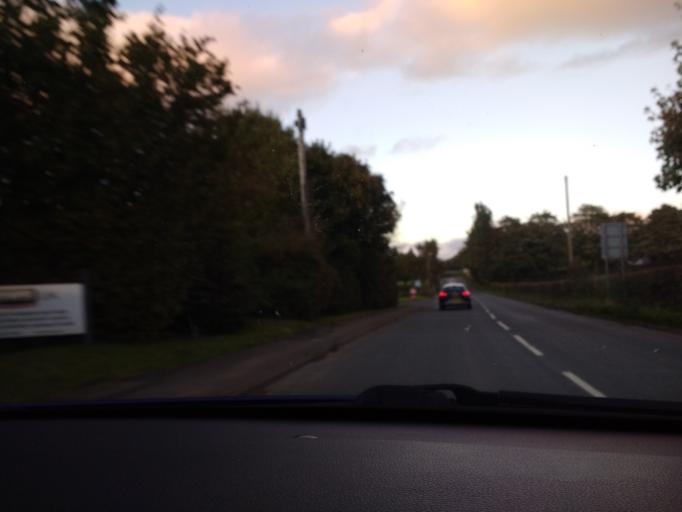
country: GB
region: England
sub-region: Lancashire
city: Caton
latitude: 54.0920
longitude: -2.6681
